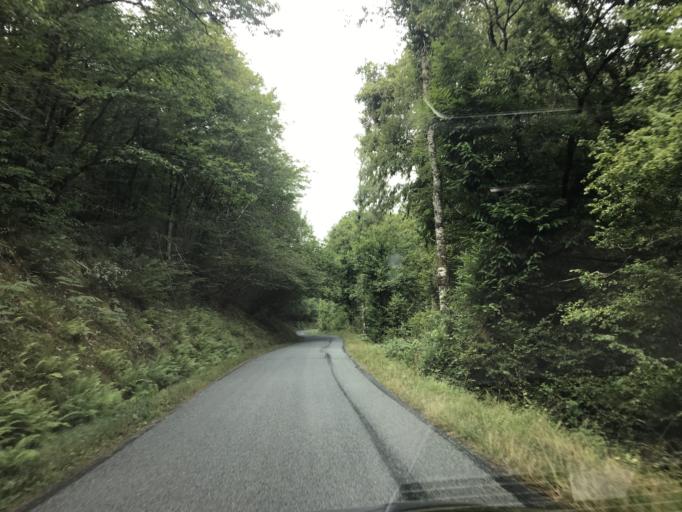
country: FR
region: Auvergne
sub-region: Departement du Cantal
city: Pleaux
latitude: 45.2414
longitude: 2.1868
